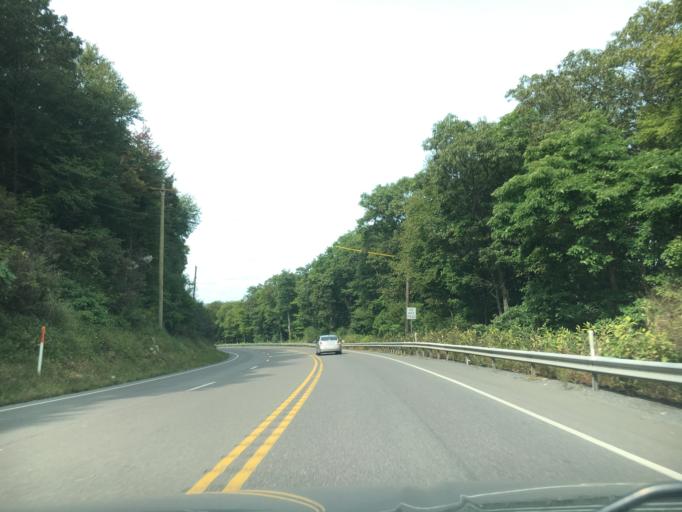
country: US
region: Pennsylvania
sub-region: Carbon County
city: Summit Hill
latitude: 40.7083
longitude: -75.8164
